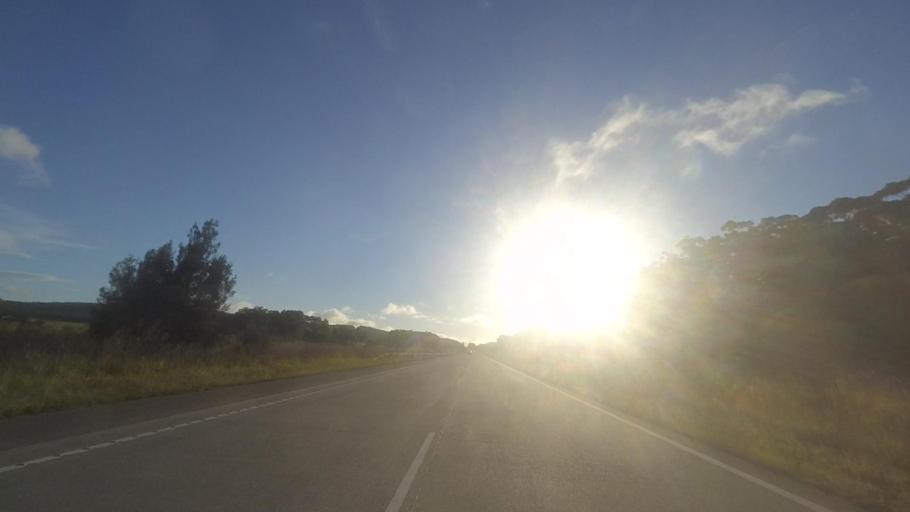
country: AU
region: New South Wales
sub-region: Great Lakes
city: Bulahdelah
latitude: -32.5229
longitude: 152.2001
